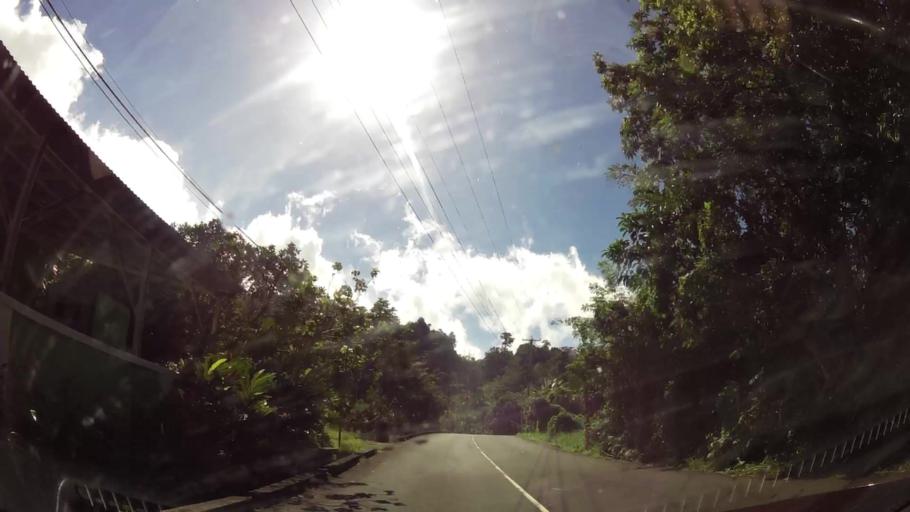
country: DM
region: Saint Paul
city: Pont Casse
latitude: 15.3649
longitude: -61.3549
